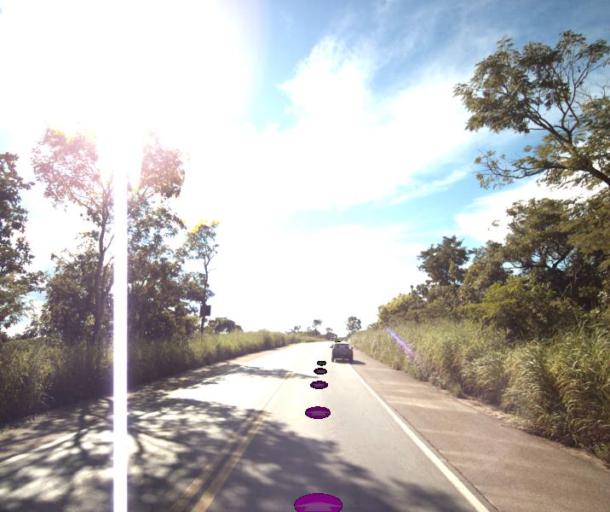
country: BR
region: Goias
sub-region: Uruana
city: Uruana
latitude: -15.5230
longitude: -49.4661
